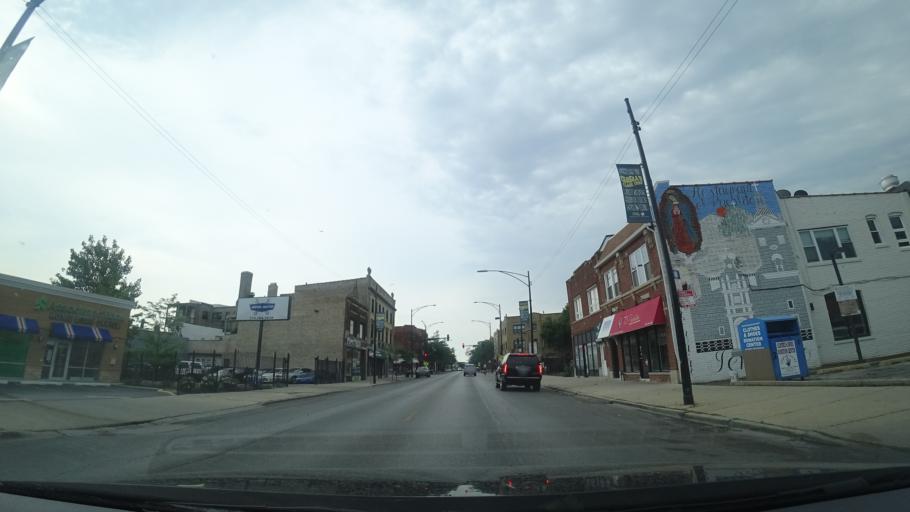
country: US
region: Illinois
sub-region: Cook County
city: Evanston
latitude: 42.0041
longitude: -87.6727
